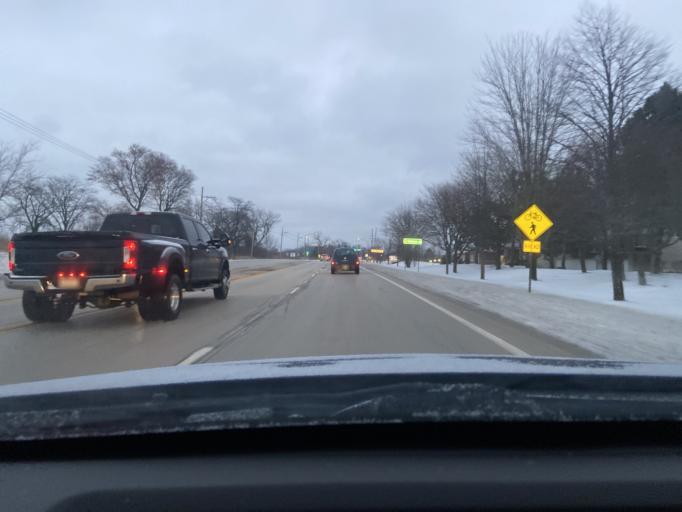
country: US
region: Illinois
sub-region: Lake County
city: Third Lake
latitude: 42.3602
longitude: -88.0272
